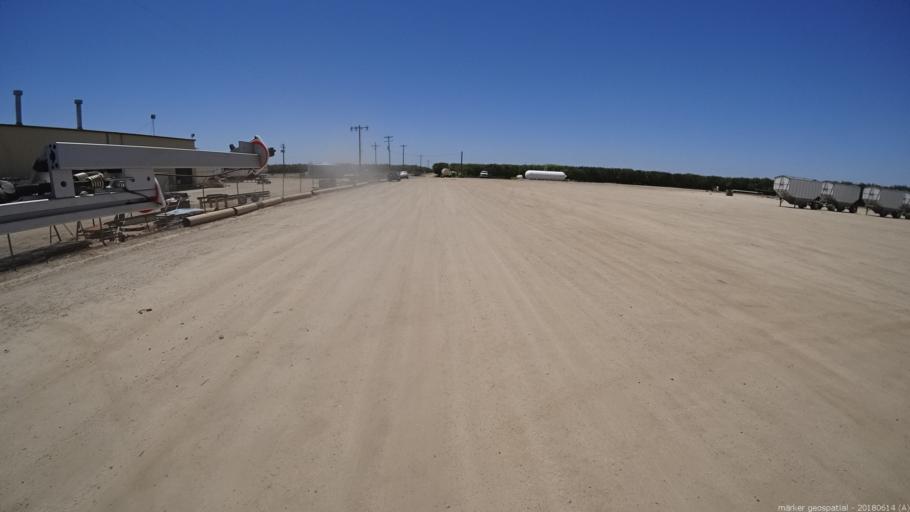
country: US
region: California
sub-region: Madera County
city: Fairmead
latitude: 37.0329
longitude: -120.2033
